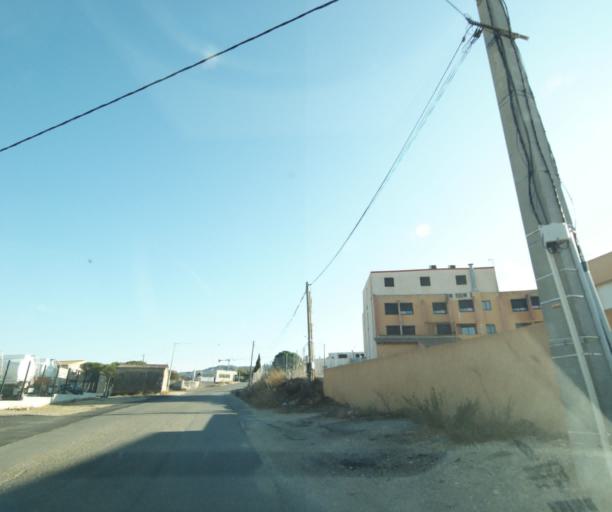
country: FR
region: Provence-Alpes-Cote d'Azur
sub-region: Departement des Bouches-du-Rhone
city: Chateauneuf-les-Martigues
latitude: 43.3954
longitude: 5.1361
